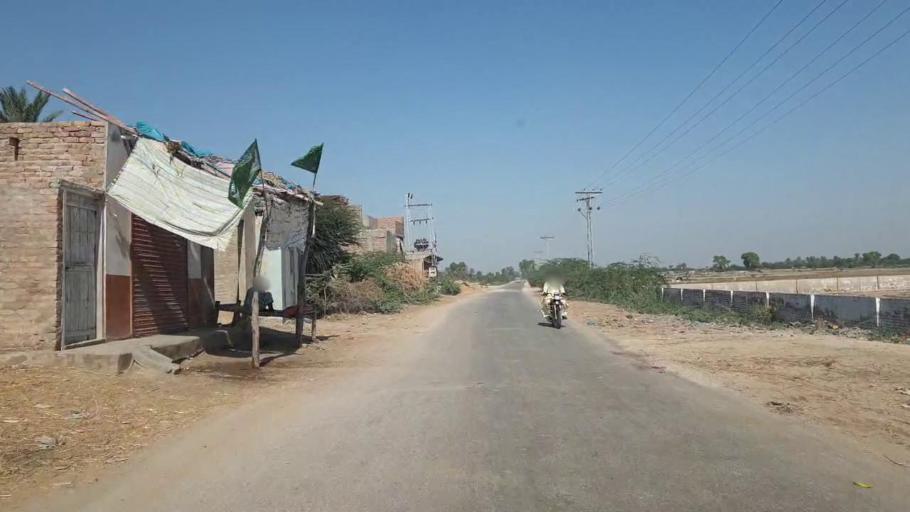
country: PK
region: Sindh
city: Talhar
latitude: 24.8872
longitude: 68.8208
